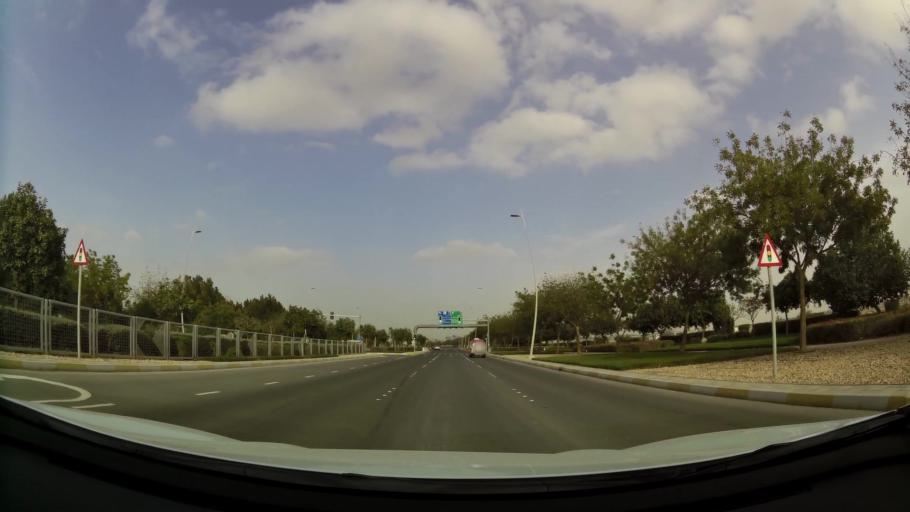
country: AE
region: Abu Dhabi
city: Abu Dhabi
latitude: 24.4850
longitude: 54.6252
